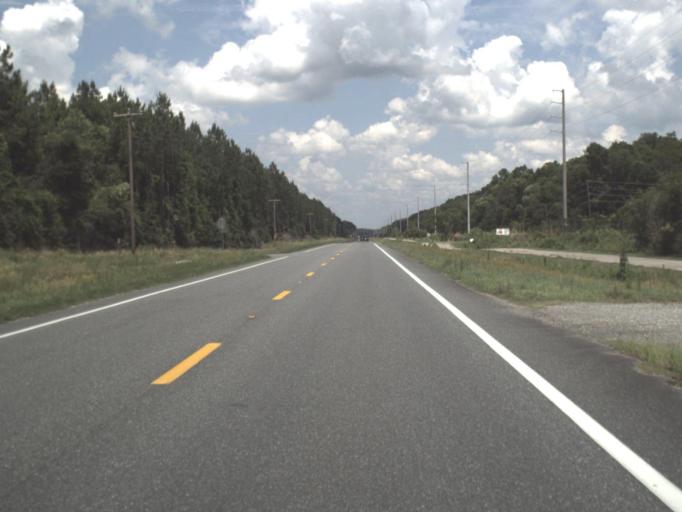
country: US
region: Florida
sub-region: Alachua County
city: High Springs
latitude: 29.9527
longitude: -82.8205
